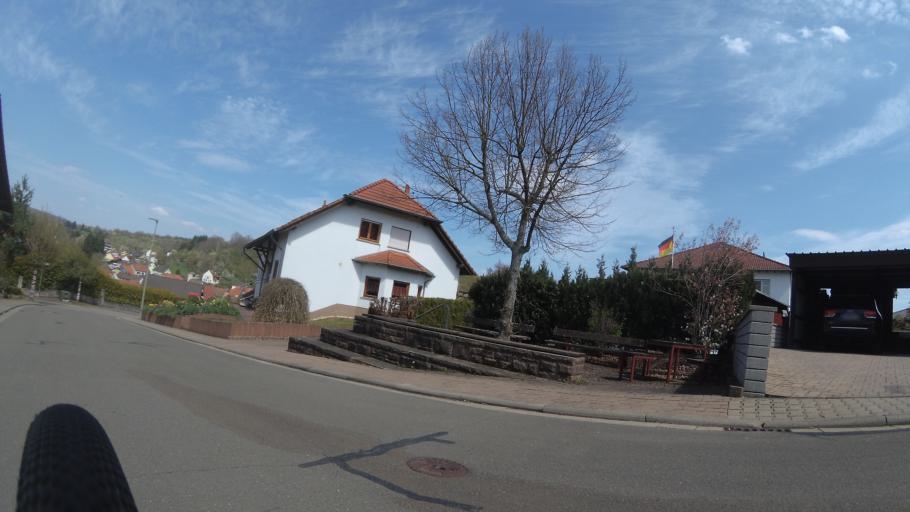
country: DE
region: Rheinland-Pfalz
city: Altenkirchen
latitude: 49.4399
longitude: 7.3215
